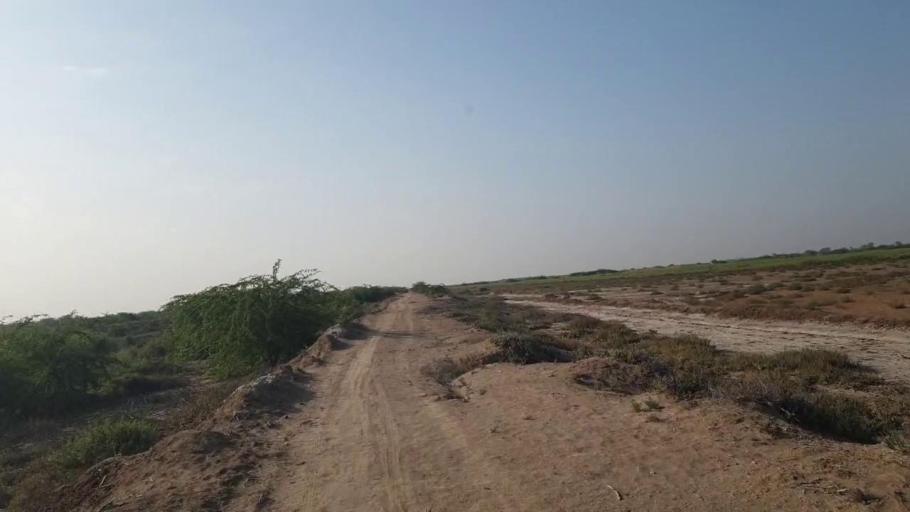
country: PK
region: Sindh
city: Badin
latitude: 24.4538
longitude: 68.7336
